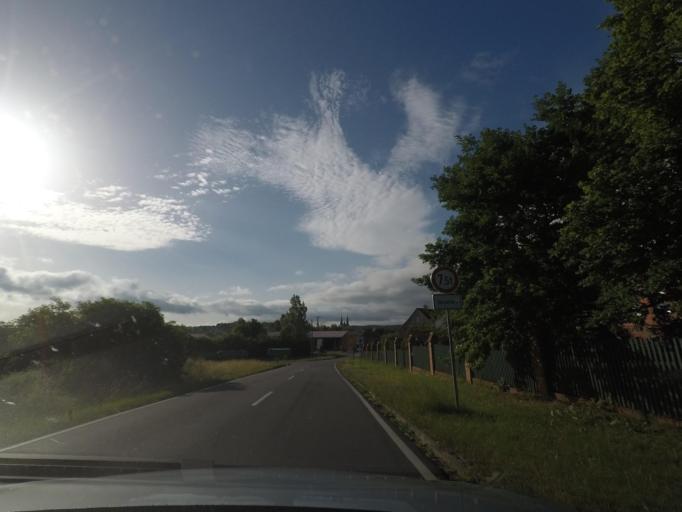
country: DE
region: Saxony-Anhalt
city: Derenburg
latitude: 51.8754
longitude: 10.9057
